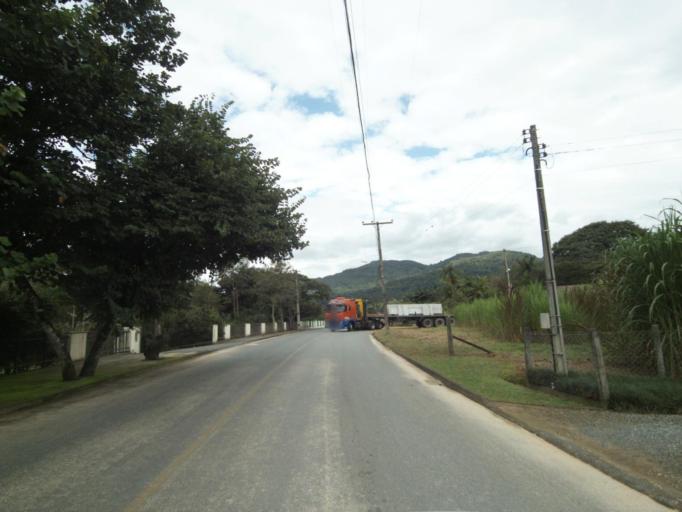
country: BR
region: Santa Catarina
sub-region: Pomerode
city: Pomerode
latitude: -26.7166
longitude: -49.2063
